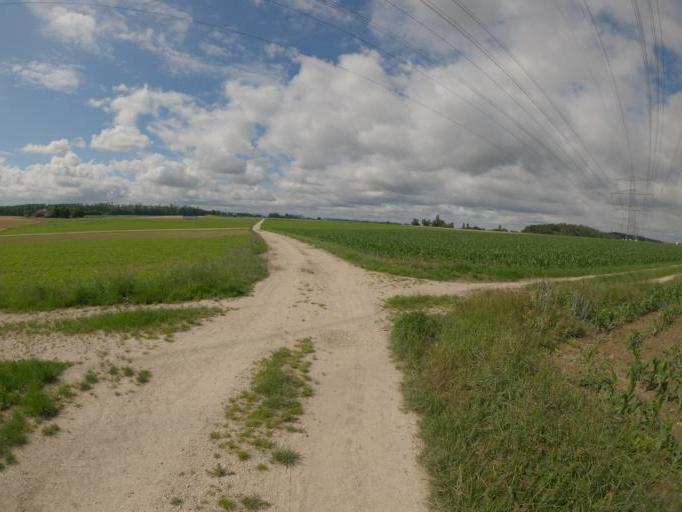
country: DE
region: Baden-Wuerttemberg
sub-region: Regierungsbezirk Stuttgart
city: Ebersbach an der Fils
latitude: 48.7008
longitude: 9.5176
